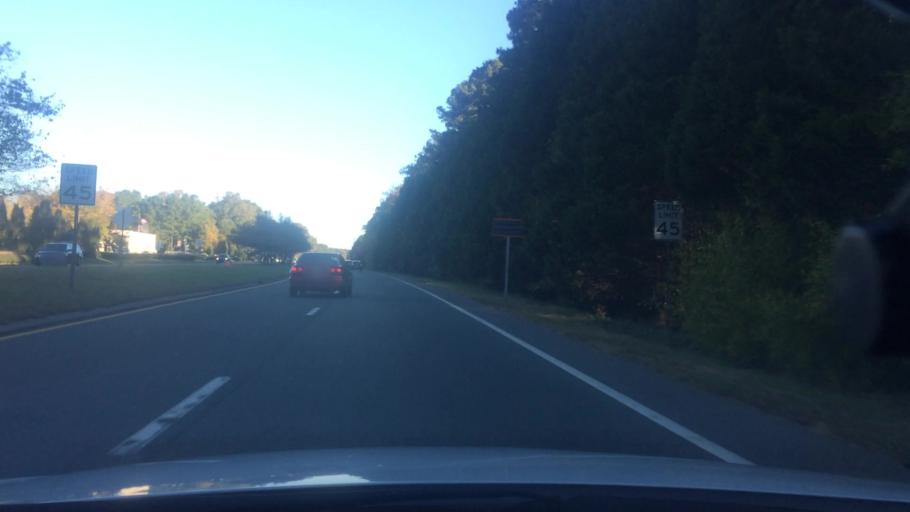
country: US
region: North Carolina
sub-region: Orange County
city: Chapel Hill
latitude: 35.9262
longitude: -79.0246
